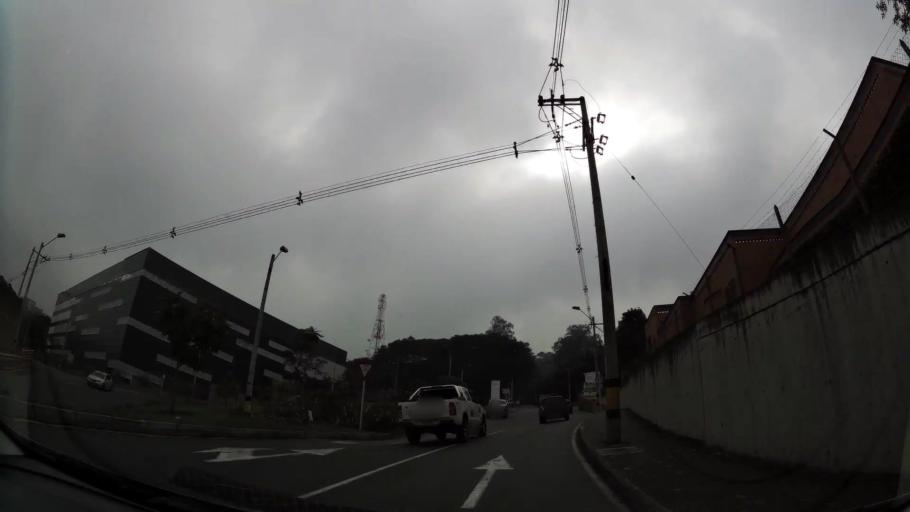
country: CO
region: Antioquia
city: Envigado
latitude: 6.1870
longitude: -75.5603
